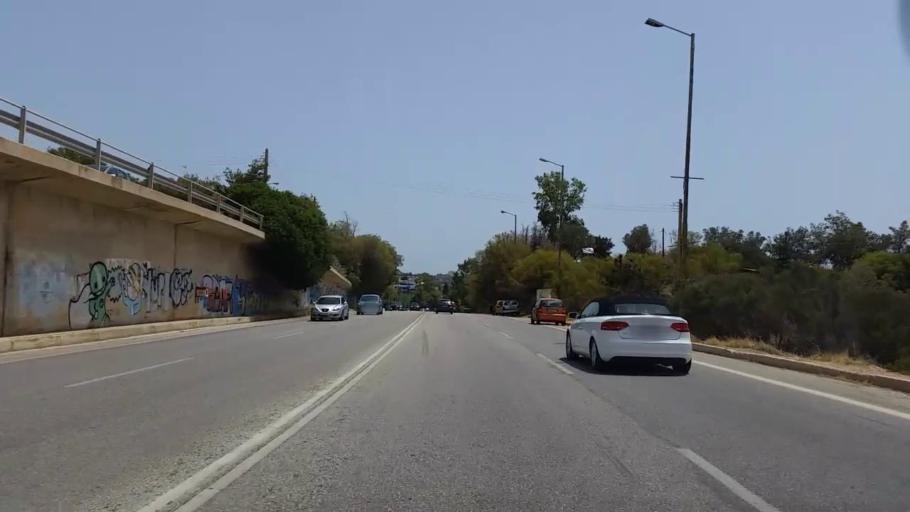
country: GR
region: Attica
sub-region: Nomarchia Anatolikis Attikis
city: Saronida
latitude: 37.7451
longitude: 23.9035
